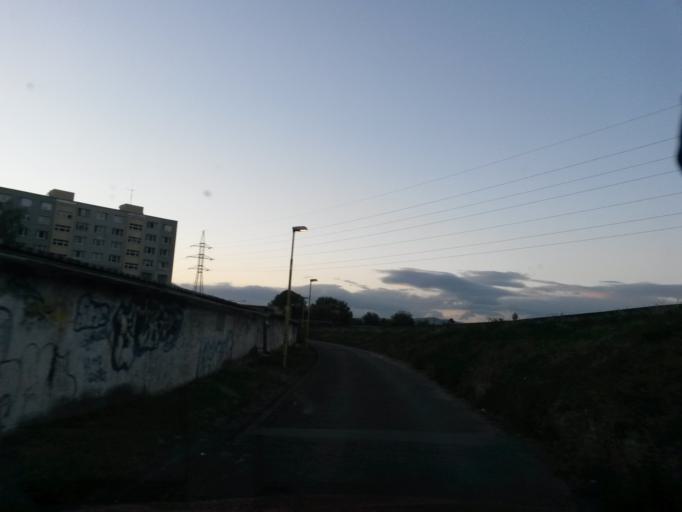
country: SK
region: Kosicky
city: Kosice
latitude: 48.6975
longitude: 21.2845
